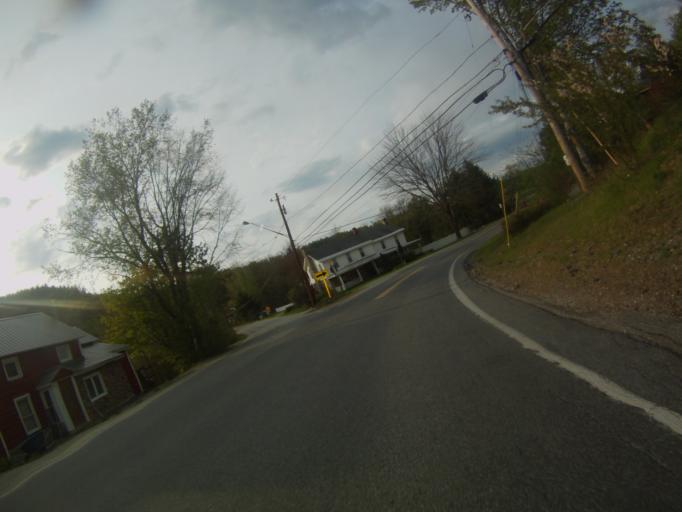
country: US
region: New York
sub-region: Warren County
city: Warrensburg
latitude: 43.6849
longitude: -73.7393
